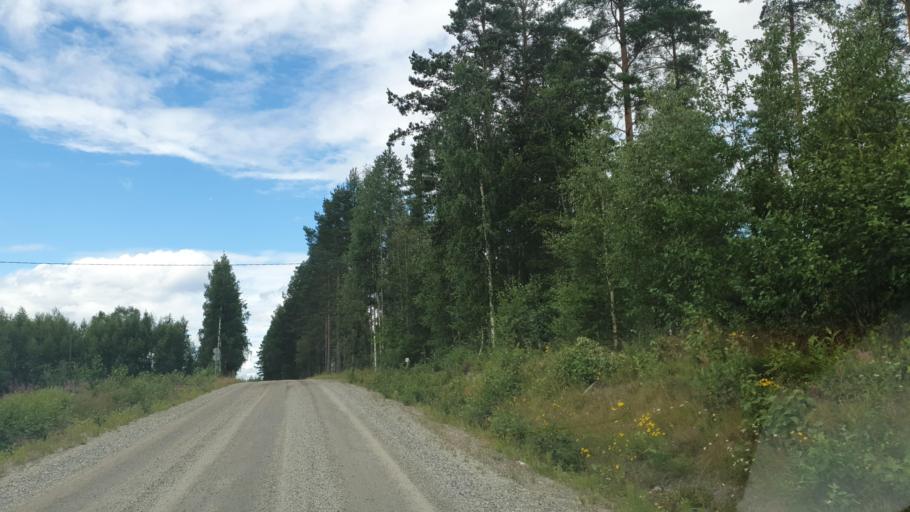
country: FI
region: Kainuu
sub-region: Kehys-Kainuu
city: Kuhmo
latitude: 64.1092
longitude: 29.3835
